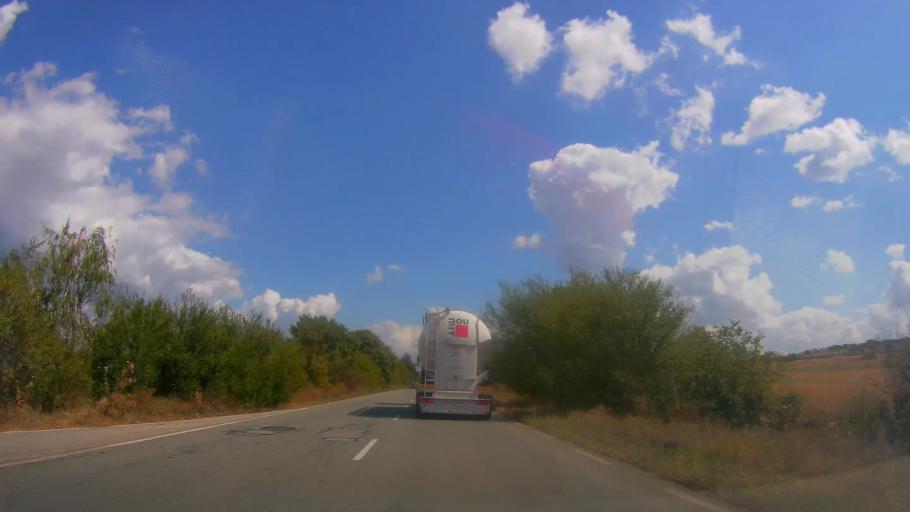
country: BG
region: Sliven
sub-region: Obshtina Tvurditsa
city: Tvurditsa
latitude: 42.6567
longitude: 25.9273
